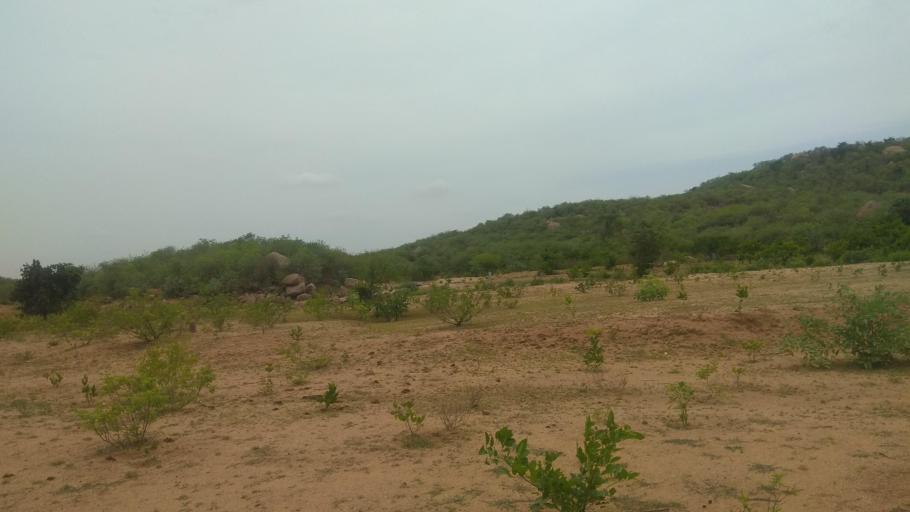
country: IN
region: Telangana
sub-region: Mahbubnagar
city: Farrukhnagar
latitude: 16.8919
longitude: 78.4876
